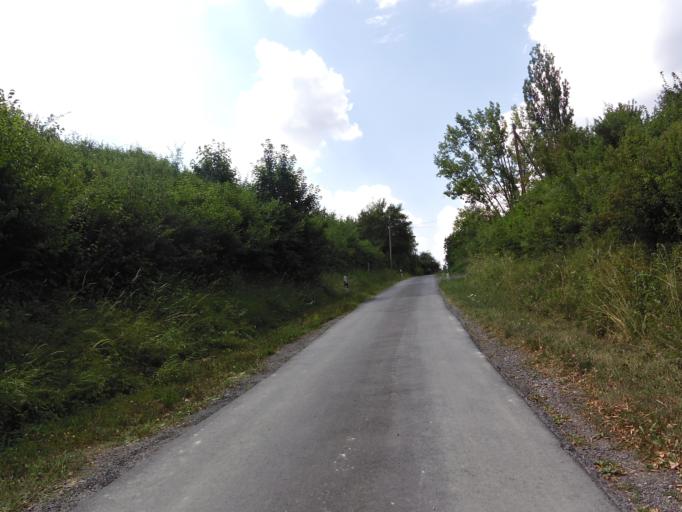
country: DE
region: Bavaria
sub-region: Regierungsbezirk Unterfranken
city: Randersacker
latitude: 49.7538
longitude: 9.9533
